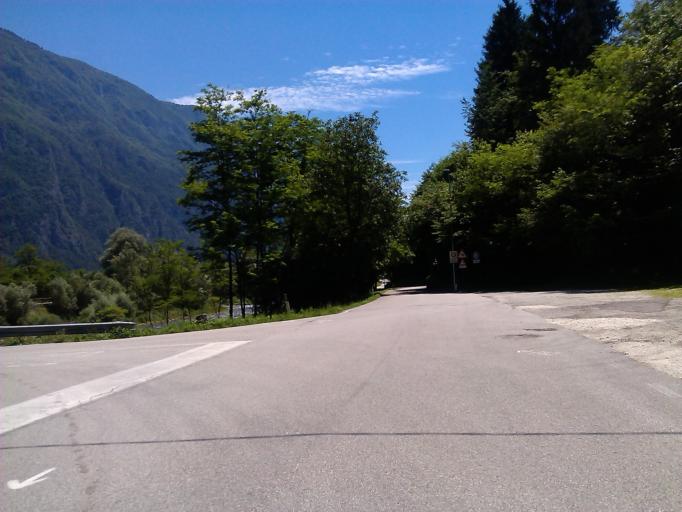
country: IT
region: Trentino-Alto Adige
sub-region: Provincia di Trento
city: Grigno
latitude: 46.0041
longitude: 11.6437
